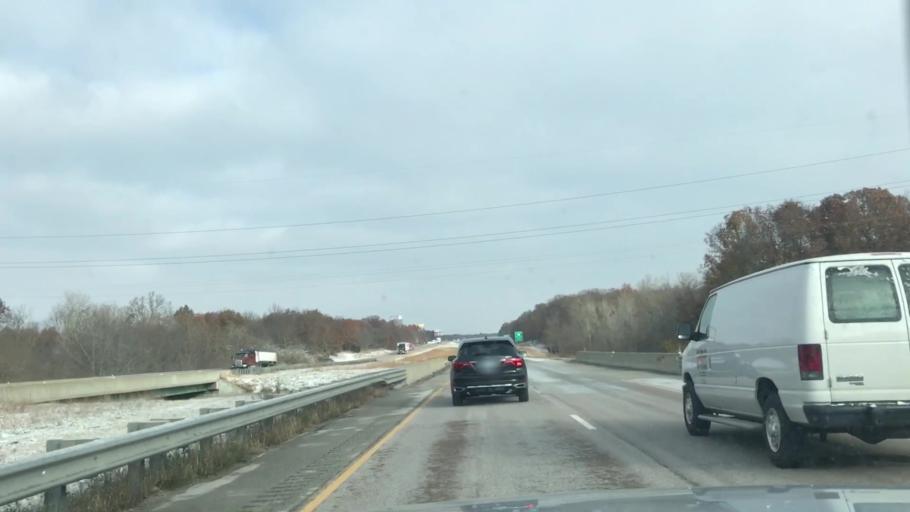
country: US
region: Illinois
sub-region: Macoupin County
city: Mount Olive
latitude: 39.0573
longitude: -89.7555
